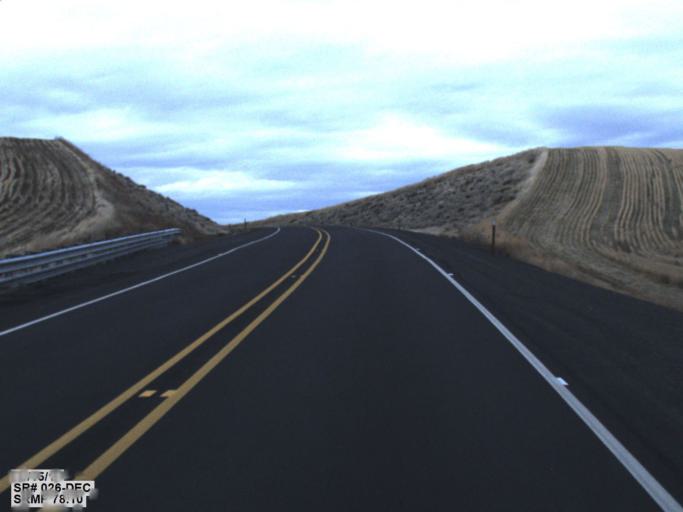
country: US
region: Washington
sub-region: Adams County
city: Ritzville
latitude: 46.7930
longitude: -118.3901
